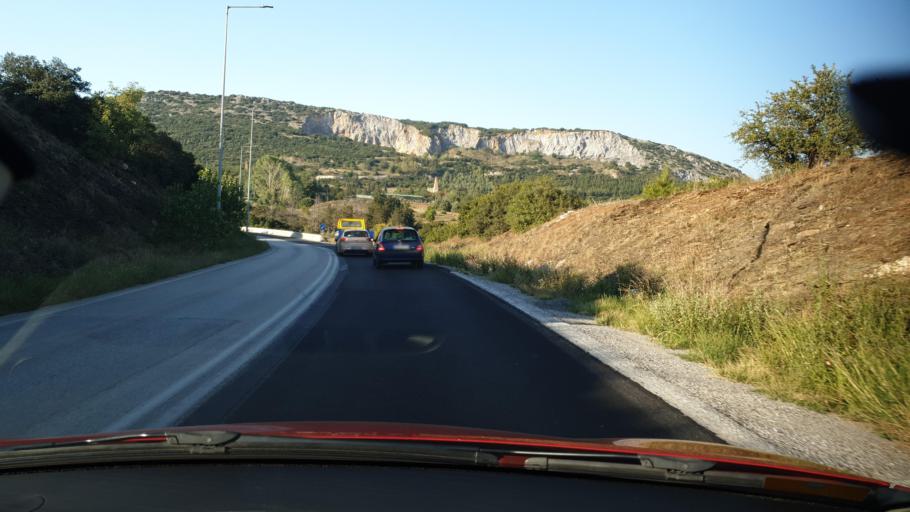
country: GR
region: Central Macedonia
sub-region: Nomos Thessalonikis
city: Chortiatis
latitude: 40.6199
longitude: 23.0649
